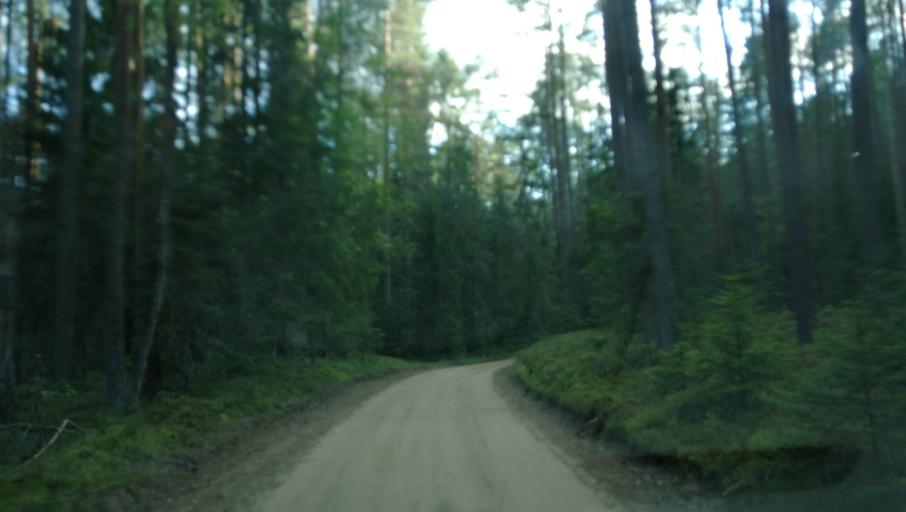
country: LV
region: Cesu Rajons
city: Cesis
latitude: 57.2936
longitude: 25.2055
